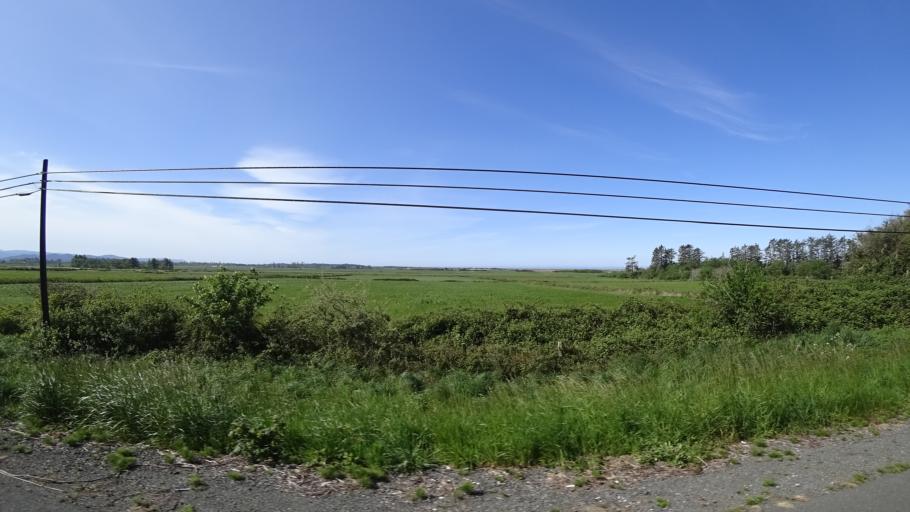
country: US
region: Oregon
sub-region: Curry County
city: Harbor
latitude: 41.9418
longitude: -124.1867
